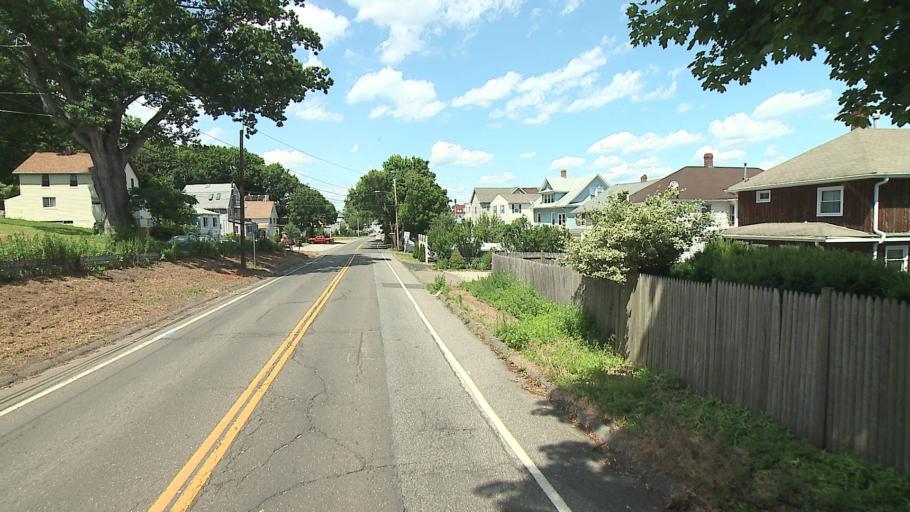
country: US
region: Connecticut
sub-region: New Haven County
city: Woodmont
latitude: 41.2192
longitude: -73.0064
